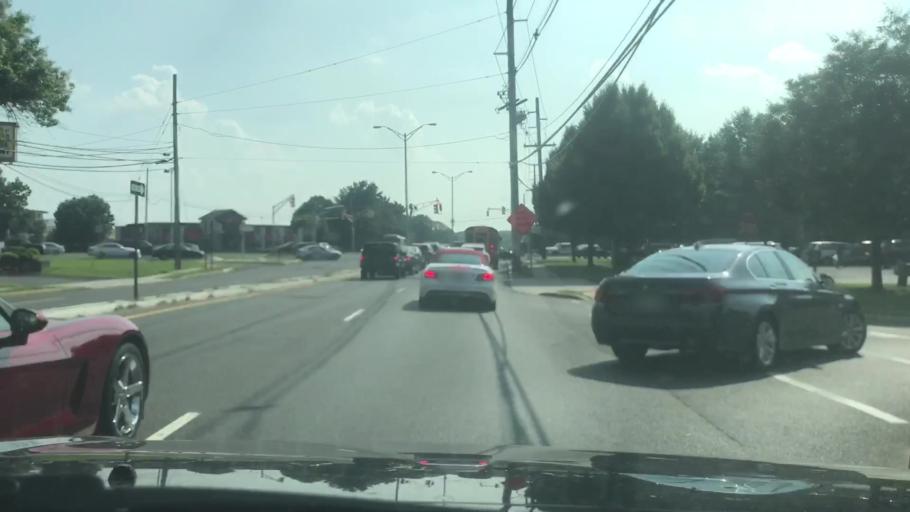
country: US
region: New Jersey
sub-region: Monmouth County
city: Eatontown
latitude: 40.2917
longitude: -74.0557
